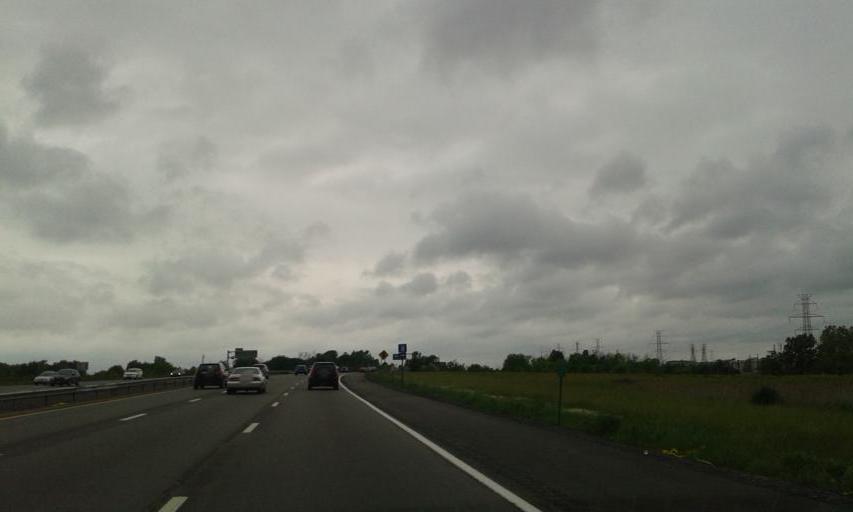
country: US
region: New York
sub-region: Erie County
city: Amherst
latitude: 42.9823
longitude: -78.7902
